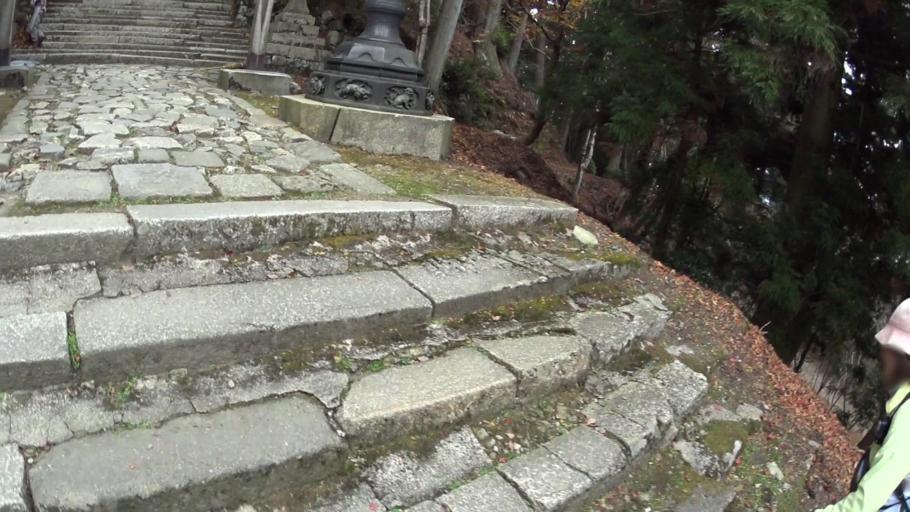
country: JP
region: Kyoto
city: Kameoka
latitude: 35.0586
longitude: 135.6346
